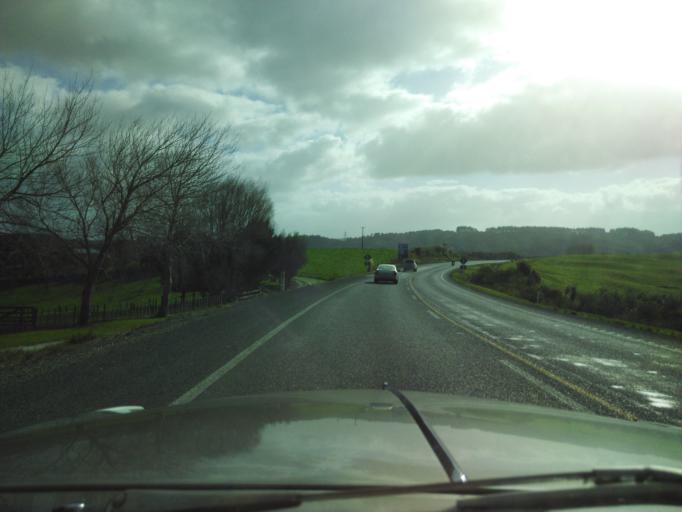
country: NZ
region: Auckland
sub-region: Auckland
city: Wellsford
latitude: -36.2213
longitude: 174.4842
